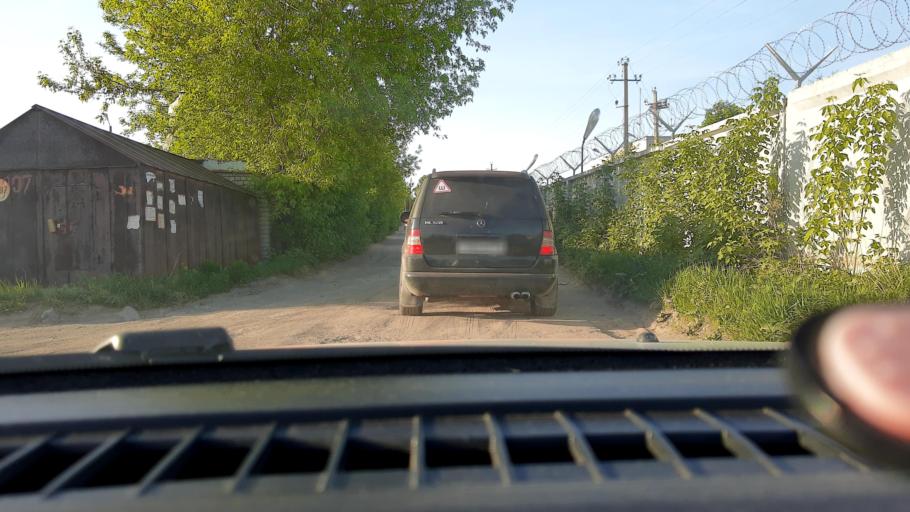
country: RU
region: Nizjnij Novgorod
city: Kstovo
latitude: 56.1344
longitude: 44.1914
